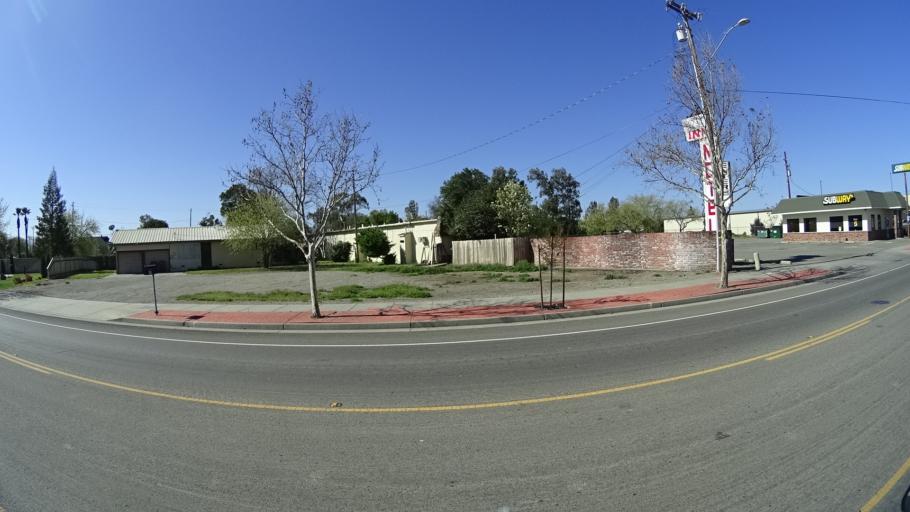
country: US
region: California
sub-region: Glenn County
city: Orland
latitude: 39.7484
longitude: -122.2000
